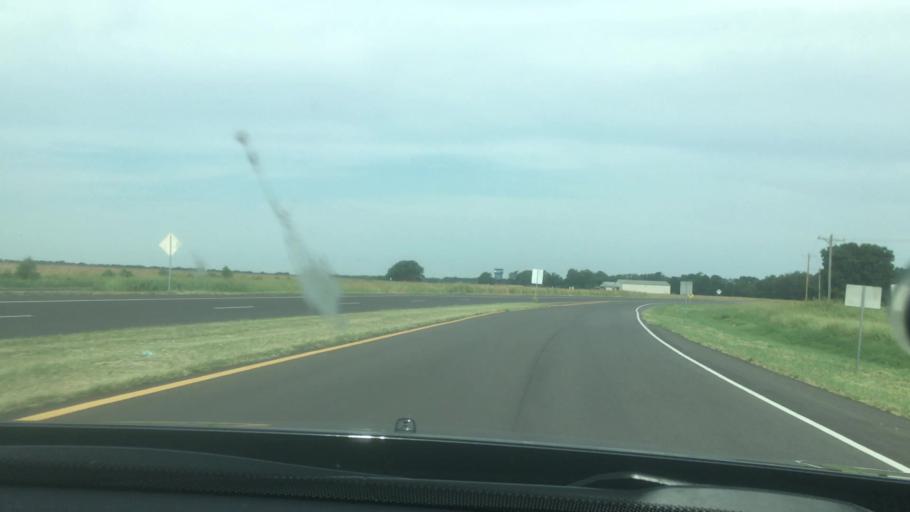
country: US
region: Oklahoma
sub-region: Garvin County
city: Pauls Valley
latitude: 34.7396
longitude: -97.2730
